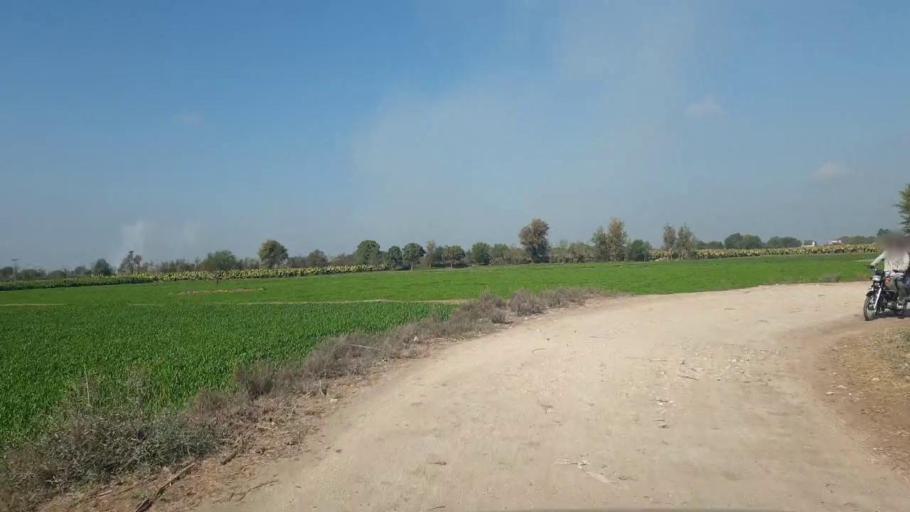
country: PK
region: Sindh
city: Shahdadpur
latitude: 25.9260
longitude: 68.5858
